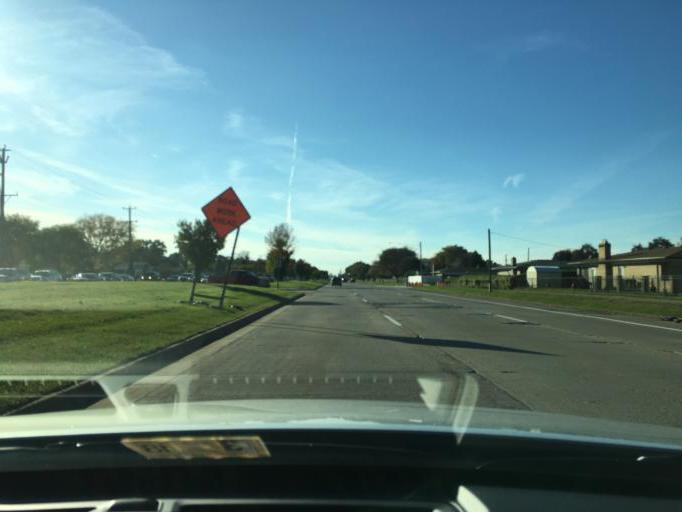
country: US
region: Michigan
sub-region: Macomb County
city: Sterling Heights
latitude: 42.5664
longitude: -83.0150
